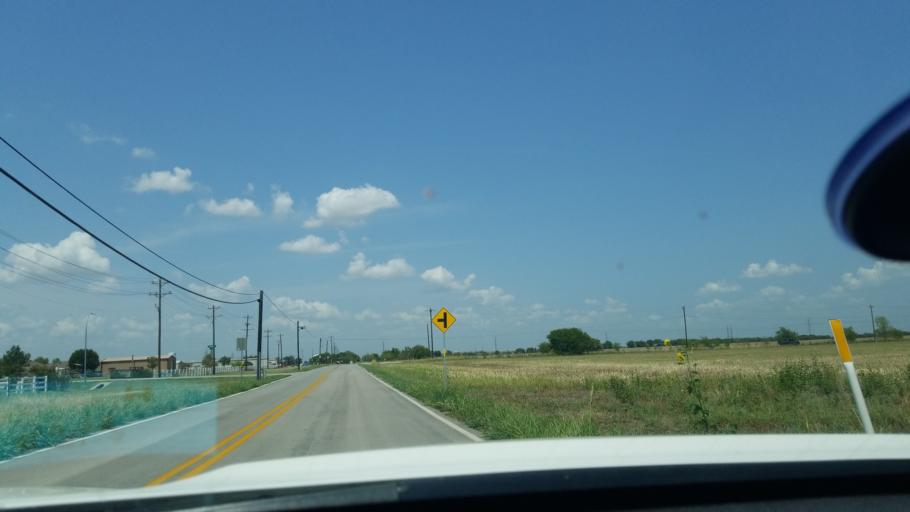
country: US
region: Texas
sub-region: Tarrant County
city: Eagle Mountain
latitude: 32.9447
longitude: -97.4093
